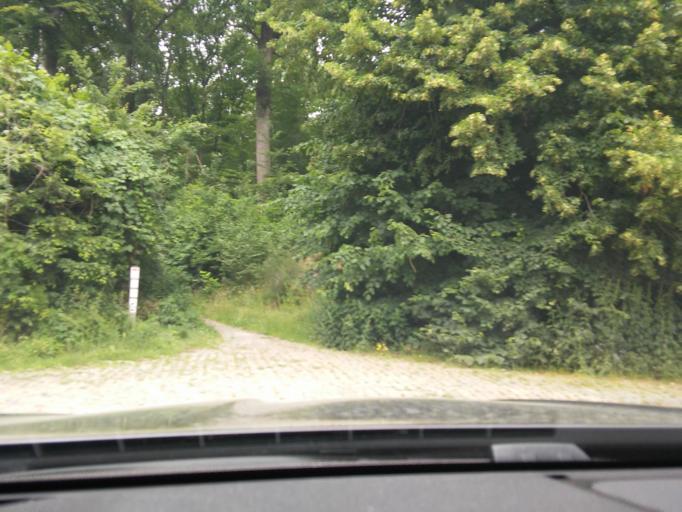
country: BE
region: Flanders
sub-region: Provincie Vlaams-Brabant
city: Oud-Heverlee
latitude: 50.8242
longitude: 4.6665
